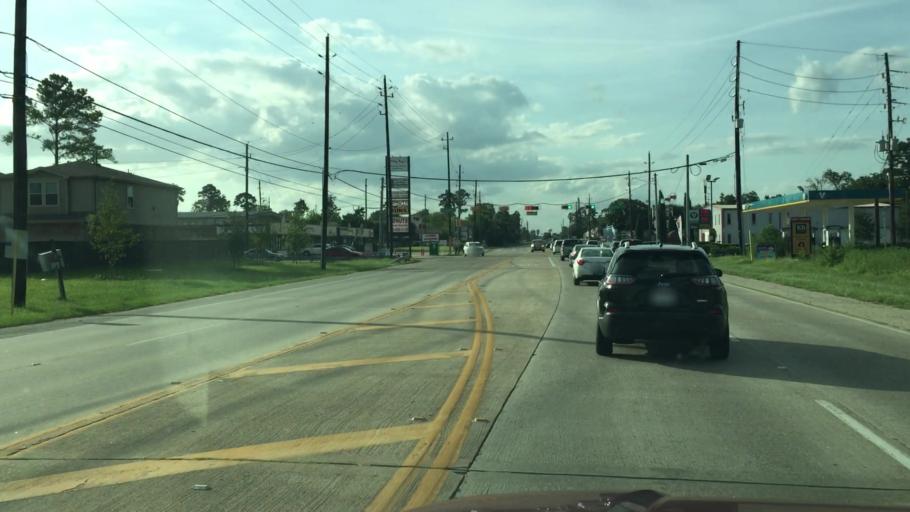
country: US
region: Texas
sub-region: Harris County
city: Hudson
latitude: 29.9982
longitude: -95.5059
